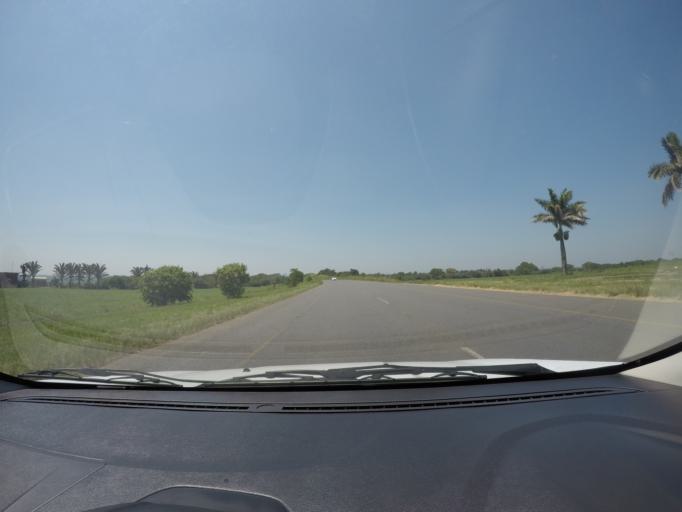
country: ZA
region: KwaZulu-Natal
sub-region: uThungulu District Municipality
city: Empangeni
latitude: -28.8029
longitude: 31.9582
